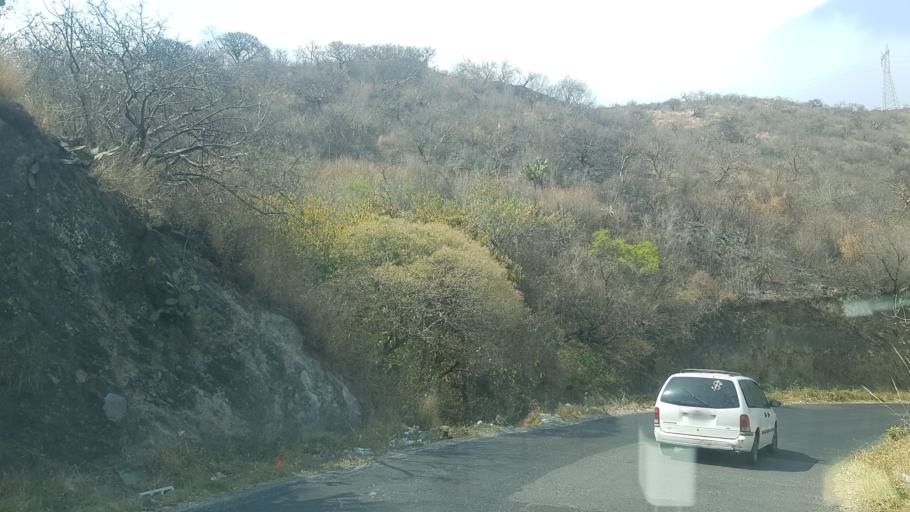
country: MX
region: Puebla
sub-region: Tianguismanalco
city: San Martin Tlapala
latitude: 18.9483
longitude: -98.4566
